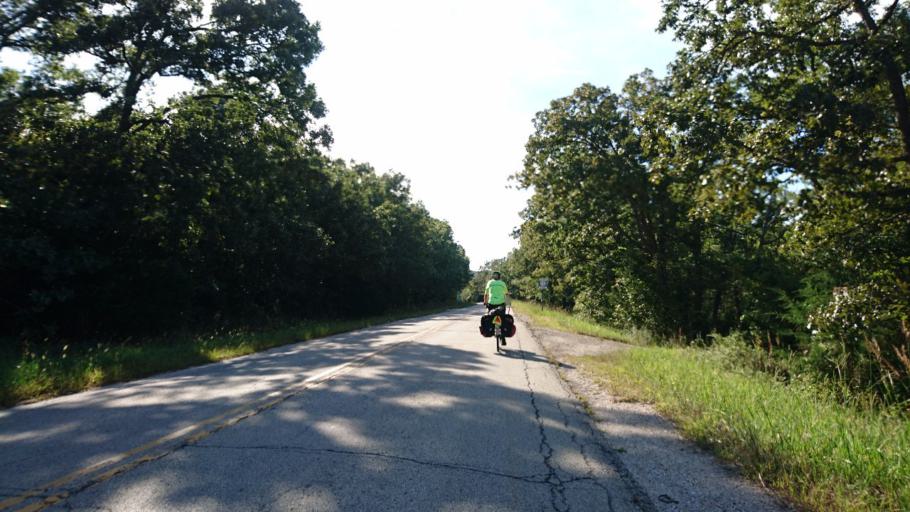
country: US
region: Missouri
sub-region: Crawford County
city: Bourbon
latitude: 38.1182
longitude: -91.3142
